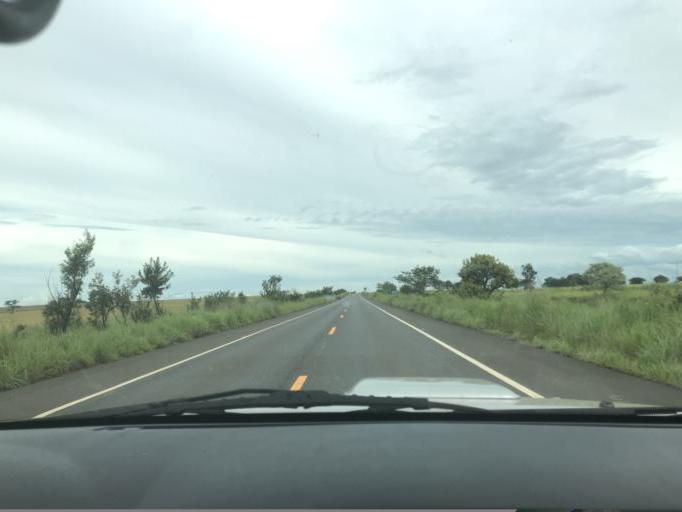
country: BR
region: Minas Gerais
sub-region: Araxa
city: Araxa
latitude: -19.3874
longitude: -46.8589
